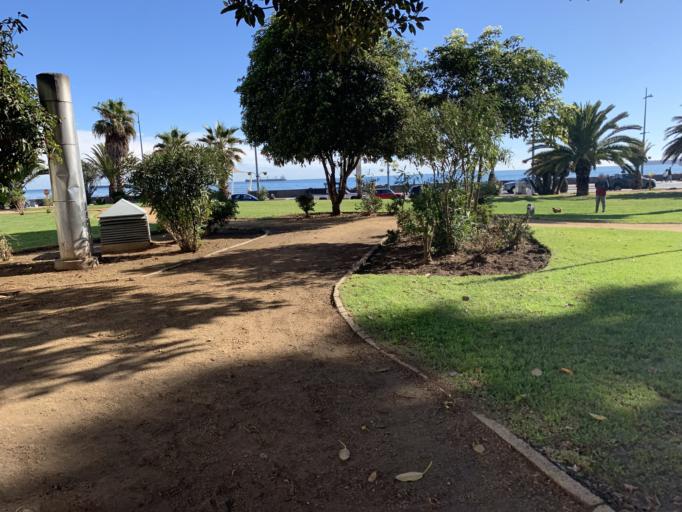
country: CL
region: Valparaiso
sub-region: Provincia de Valparaiso
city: Vina del Mar
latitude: -33.0183
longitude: -71.5604
